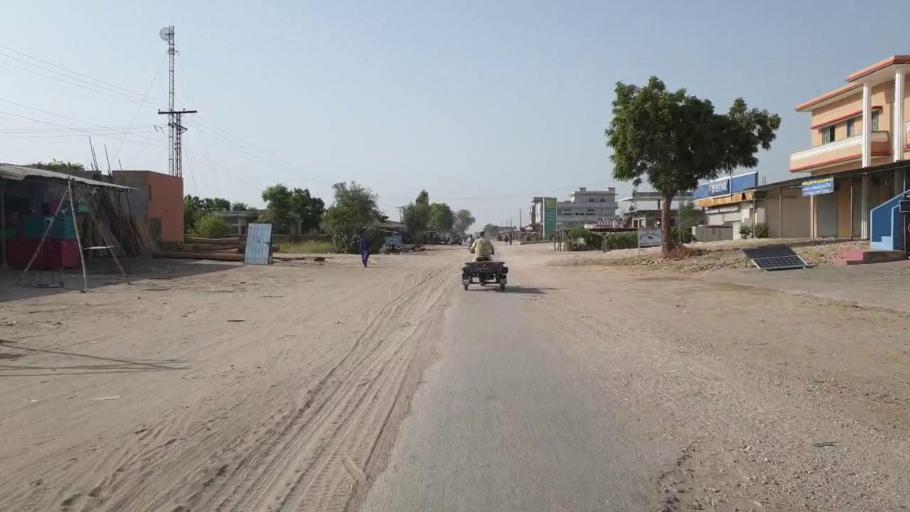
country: PK
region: Sindh
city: Sanghar
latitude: 26.2742
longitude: 68.9300
